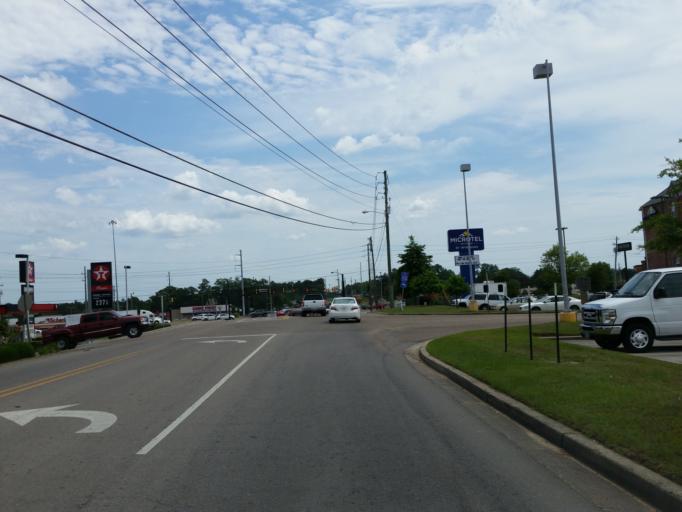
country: US
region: Mississippi
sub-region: Lamar County
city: Arnold Line
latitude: 31.3262
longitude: -89.3564
